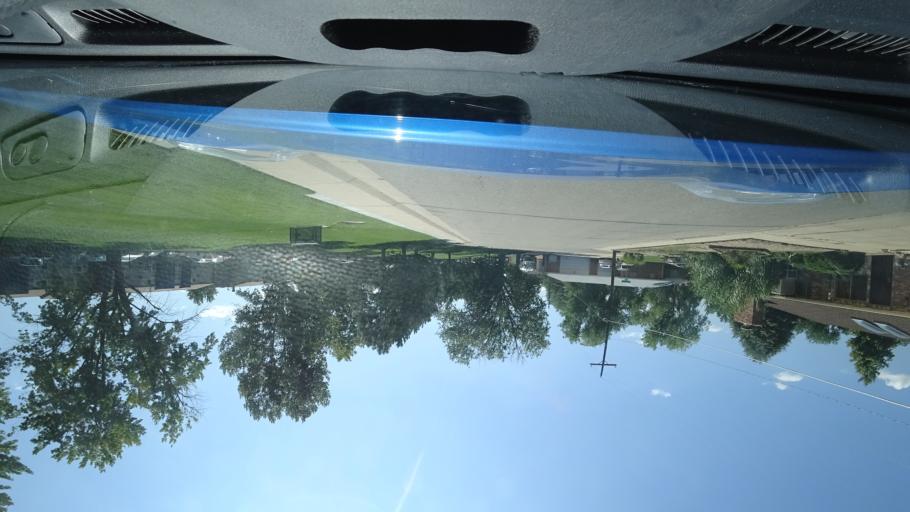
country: US
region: Colorado
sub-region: Adams County
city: Aurora
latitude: 39.7201
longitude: -104.8731
